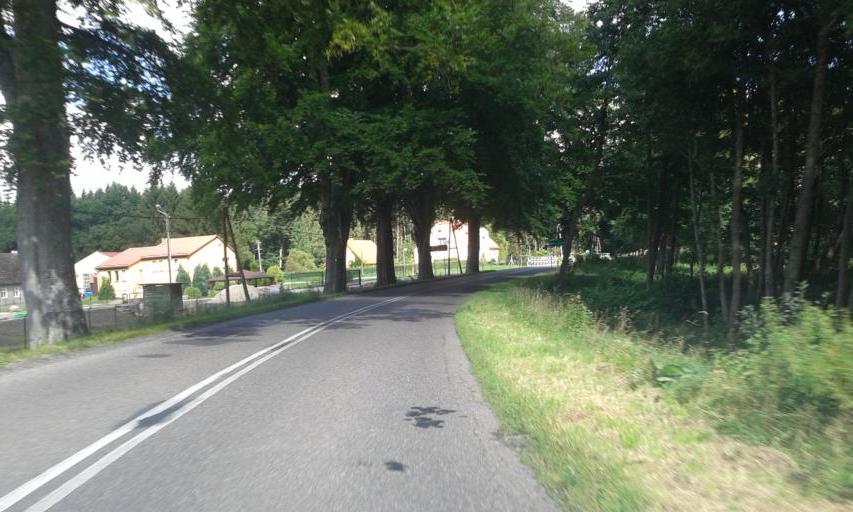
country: PL
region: West Pomeranian Voivodeship
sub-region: Powiat slawienski
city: Slawno
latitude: 54.2500
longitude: 16.6879
